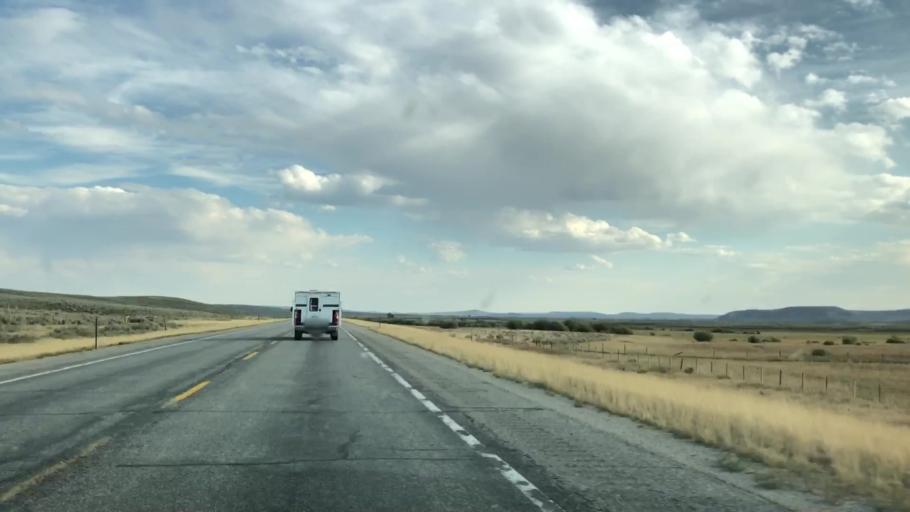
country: US
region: Wyoming
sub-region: Sublette County
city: Pinedale
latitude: 43.0278
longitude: -110.1257
